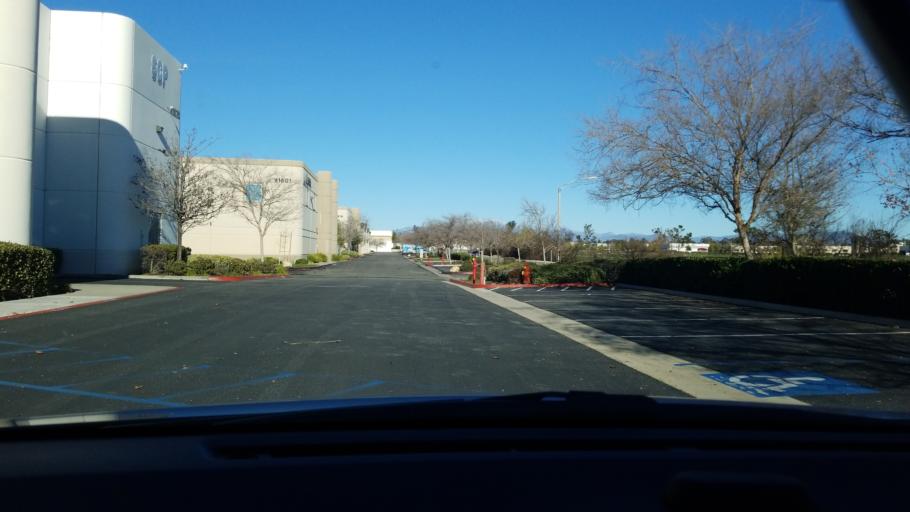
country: US
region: California
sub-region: Riverside County
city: Murrieta Hot Springs
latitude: 33.5250
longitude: -117.1753
